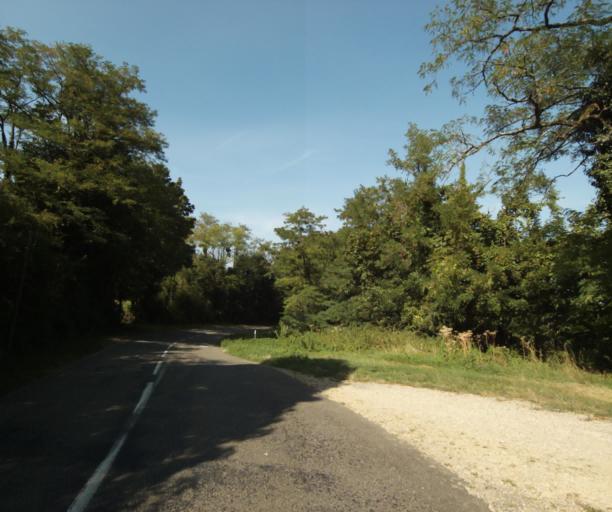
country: FR
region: Bourgogne
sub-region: Departement de Saone-et-Loire
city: Tournus
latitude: 46.5591
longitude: 4.8776
